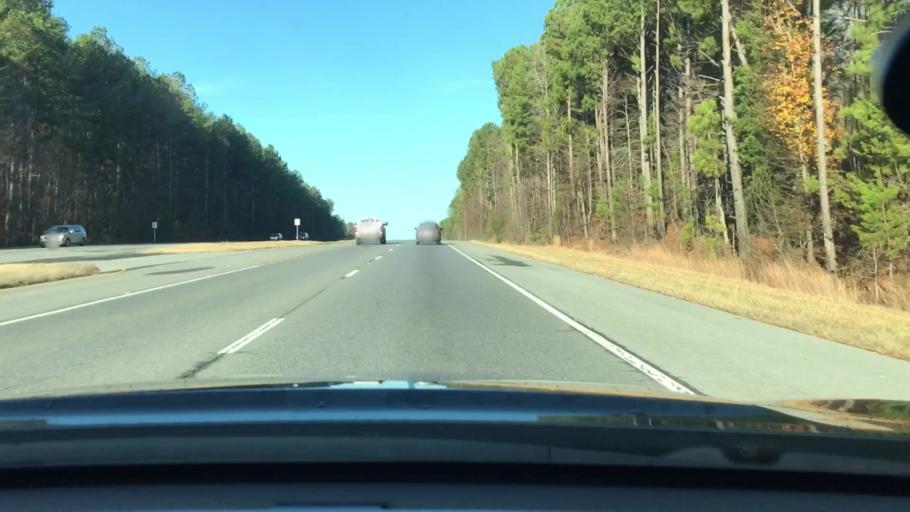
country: US
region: Alabama
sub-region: Shelby County
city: Harpersville
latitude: 33.3538
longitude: -86.4813
